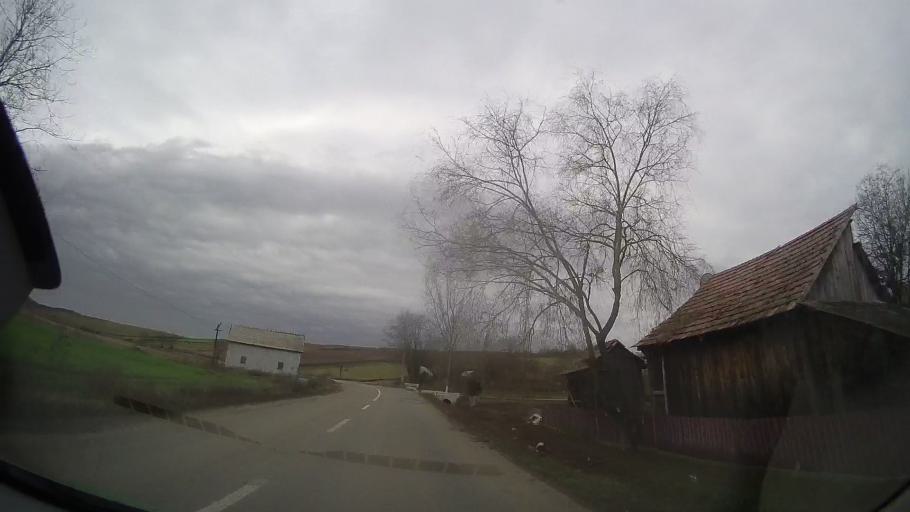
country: RO
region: Bistrita-Nasaud
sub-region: Comuna Milas
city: Milas
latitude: 46.7942
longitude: 24.4217
